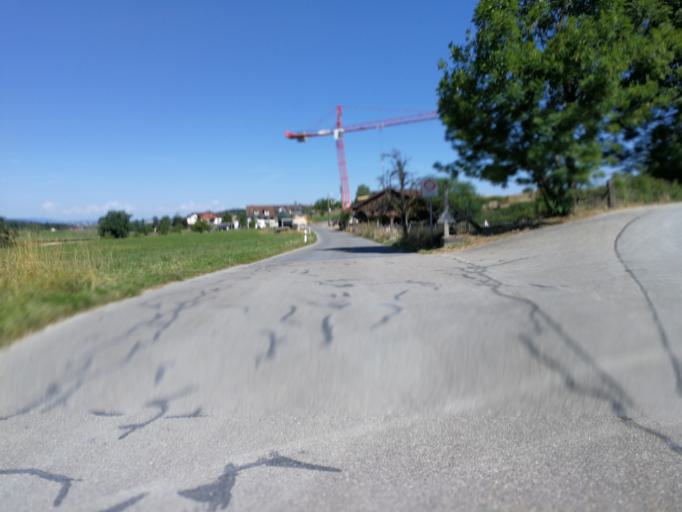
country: CH
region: Zurich
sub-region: Bezirk Hinwil
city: Gossau
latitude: 47.3142
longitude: 8.7518
